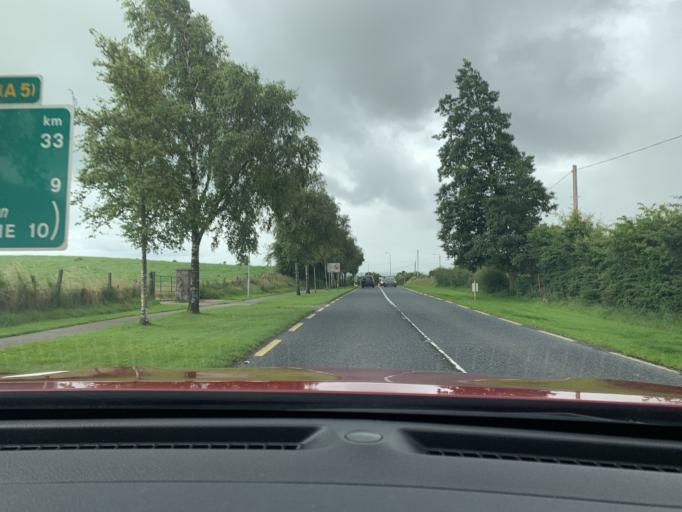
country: IE
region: Ulster
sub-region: County Donegal
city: Raphoe
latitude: 54.8017
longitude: -7.5834
